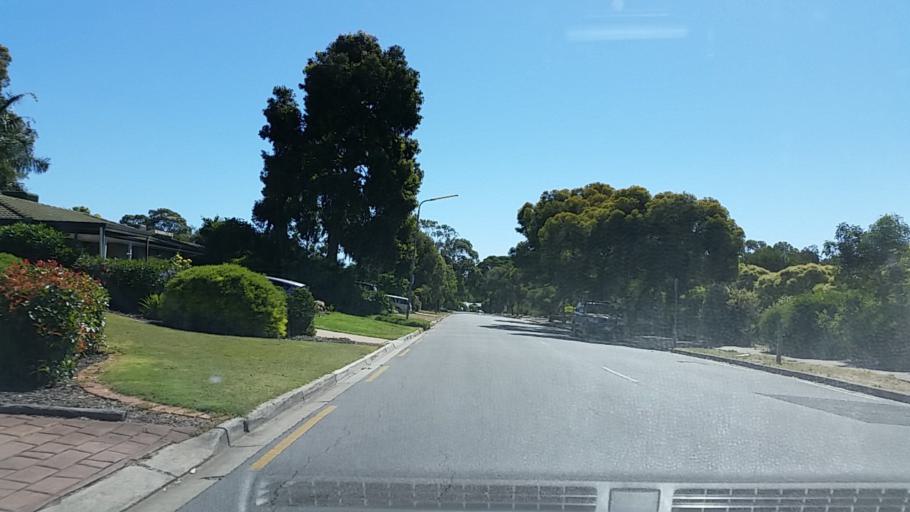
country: AU
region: South Australia
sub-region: Tea Tree Gully
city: Hope Valley
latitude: -34.8025
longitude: 138.7005
